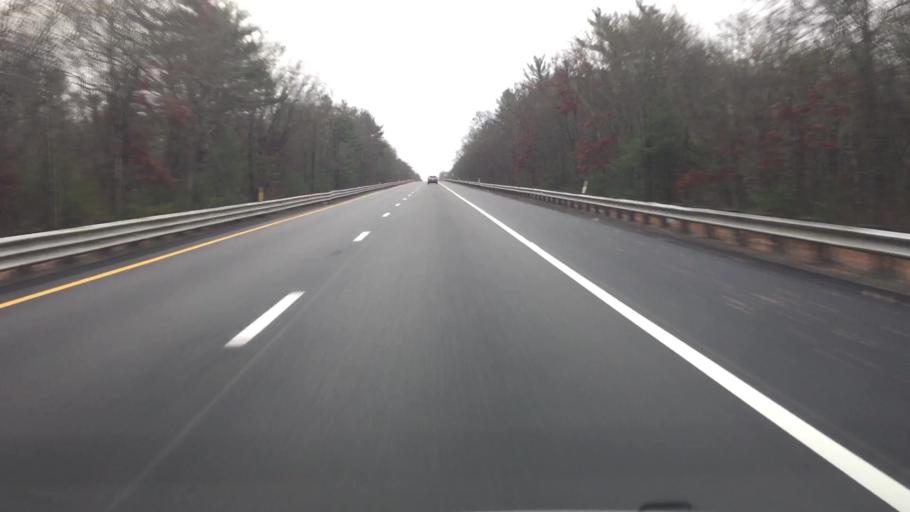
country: US
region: Massachusetts
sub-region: Plymouth County
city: West Wareham
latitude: 41.8272
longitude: -70.8120
